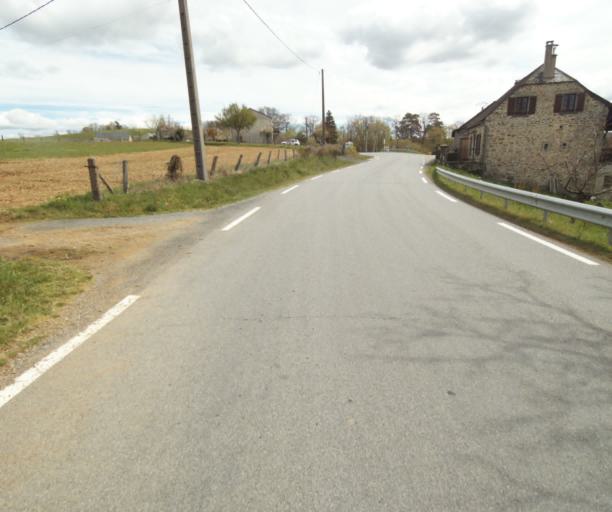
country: FR
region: Limousin
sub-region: Departement de la Correze
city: Sainte-Fortunade
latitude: 45.2010
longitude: 1.8528
